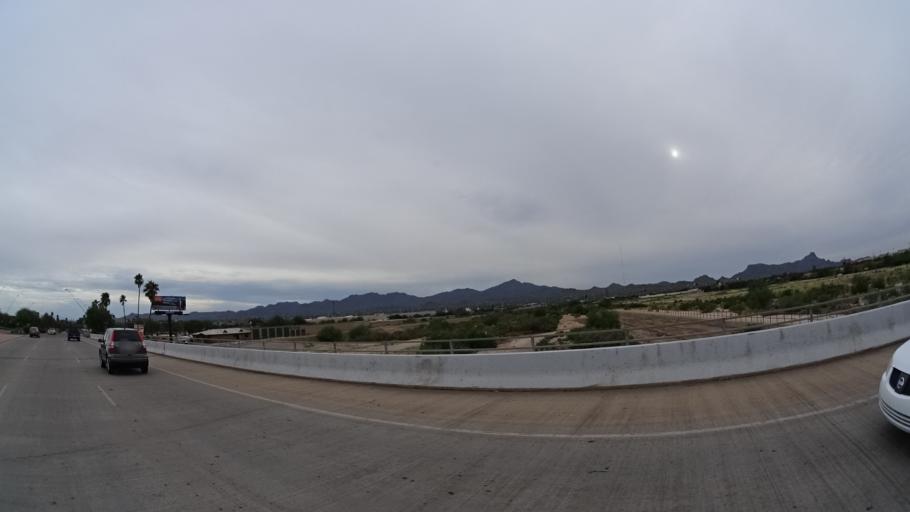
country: US
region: Arizona
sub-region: Pima County
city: Casas Adobes
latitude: 32.3341
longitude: -111.0467
